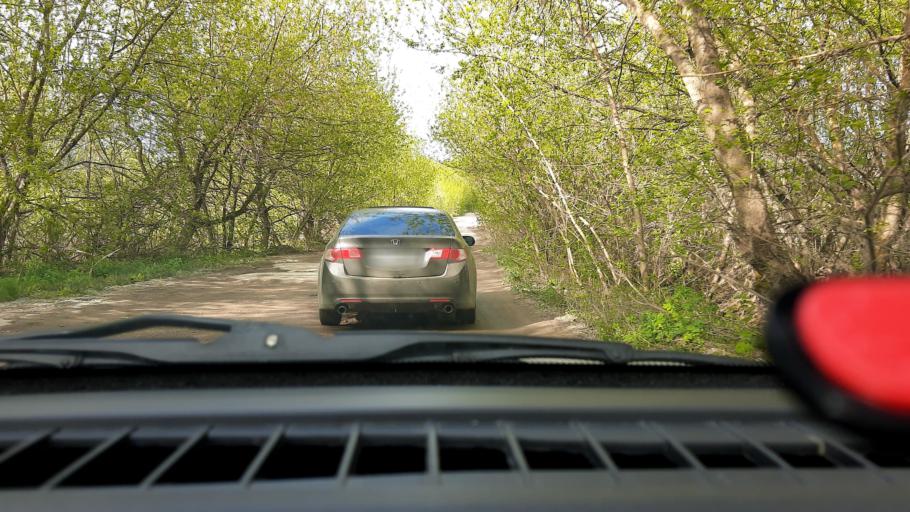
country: RU
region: Nizjnij Novgorod
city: Neklyudovo
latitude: 56.3939
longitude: 43.8468
